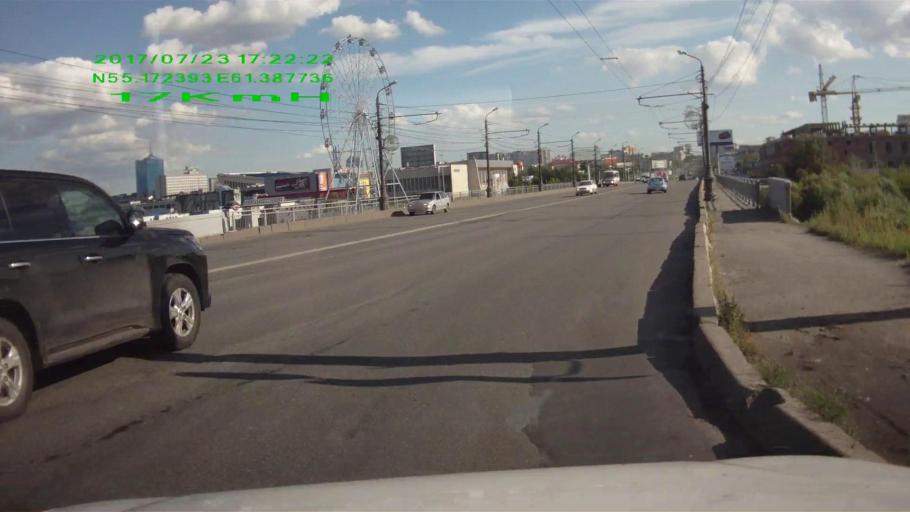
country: RU
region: Chelyabinsk
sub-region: Gorod Chelyabinsk
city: Chelyabinsk
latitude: 55.1723
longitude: 61.3878
